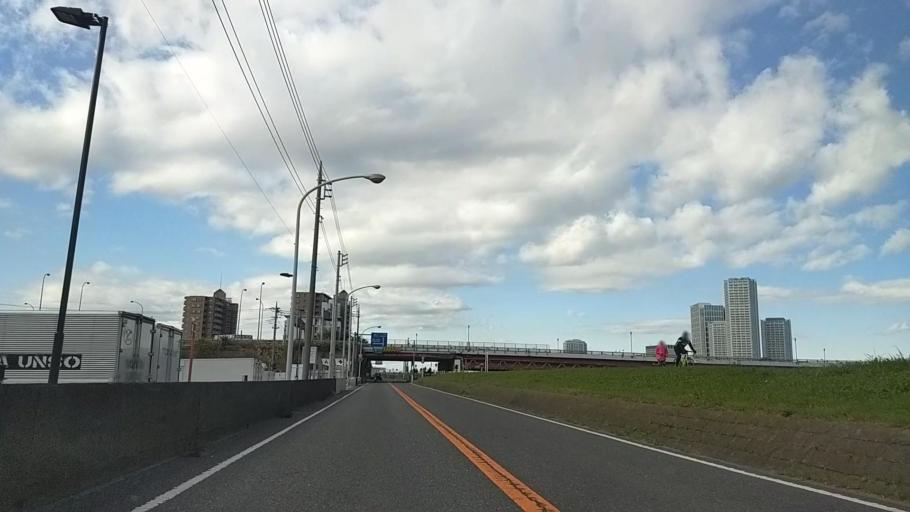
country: JP
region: Tokyo
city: Tokyo
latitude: 35.6002
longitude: 139.6357
